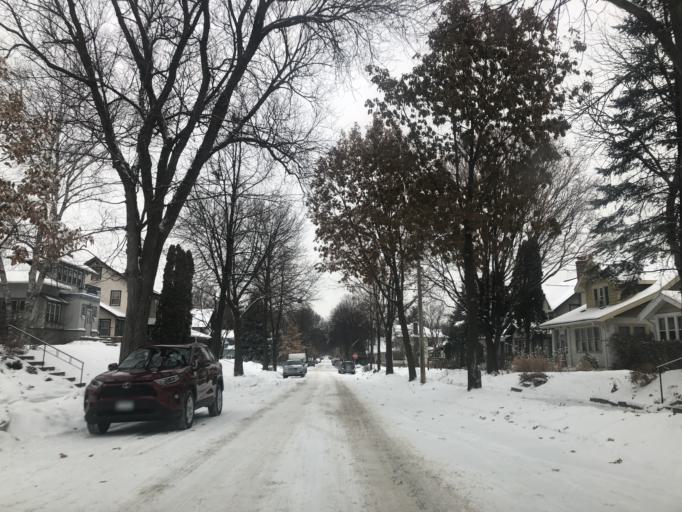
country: US
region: Minnesota
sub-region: Hennepin County
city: Richfield
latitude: 44.9295
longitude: -93.2857
